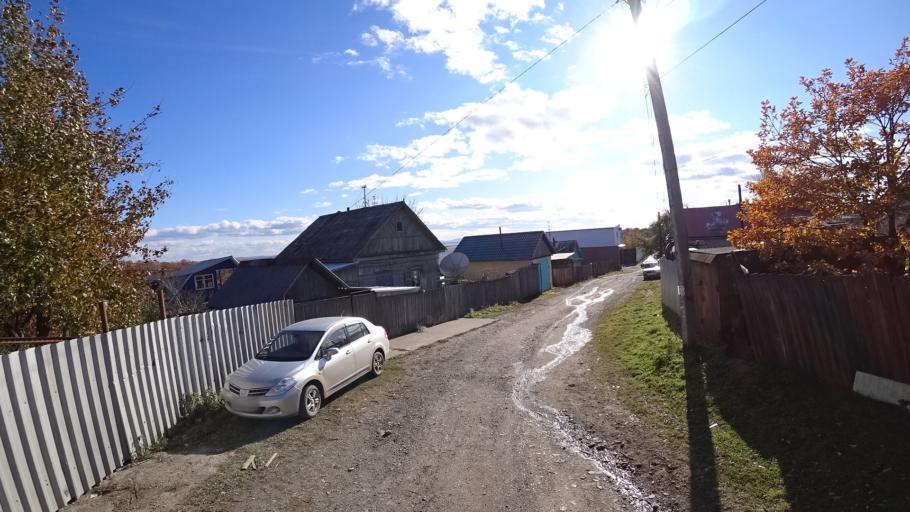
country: RU
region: Khabarovsk Krai
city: Amursk
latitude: 50.2336
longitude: 136.9213
